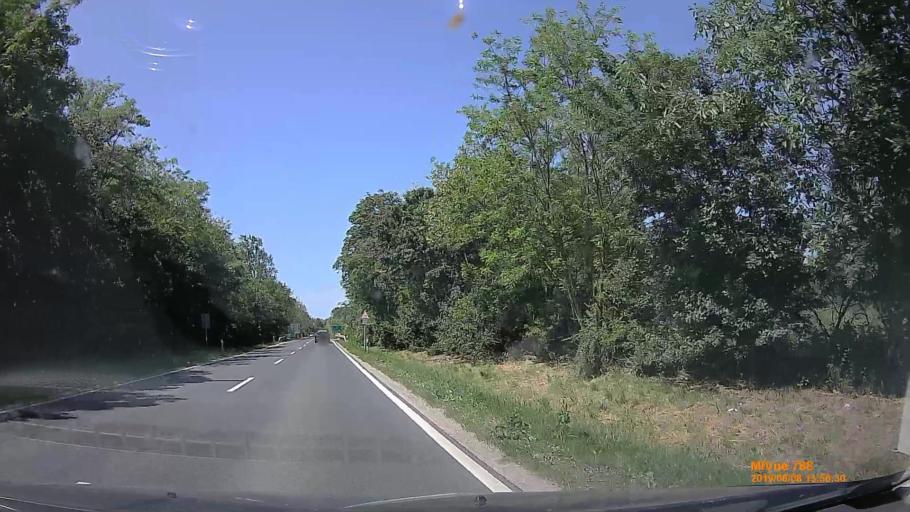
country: HU
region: Vas
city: Sarvar
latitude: 47.3627
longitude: 16.8952
